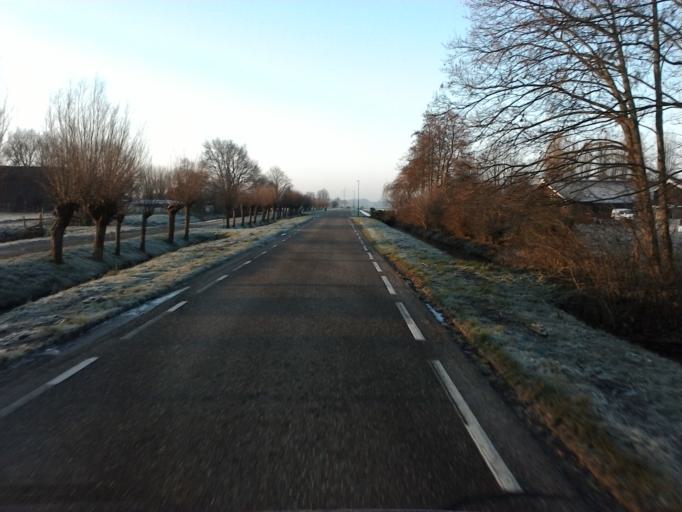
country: NL
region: South Holland
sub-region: Gemeente Gorinchem
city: Gorinchem
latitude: 51.8674
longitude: 4.9695
